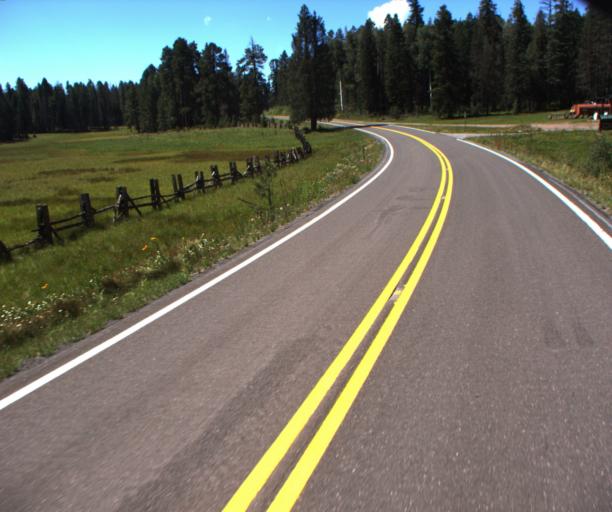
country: US
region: Arizona
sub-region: Apache County
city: Eagar
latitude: 33.6400
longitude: -109.3266
